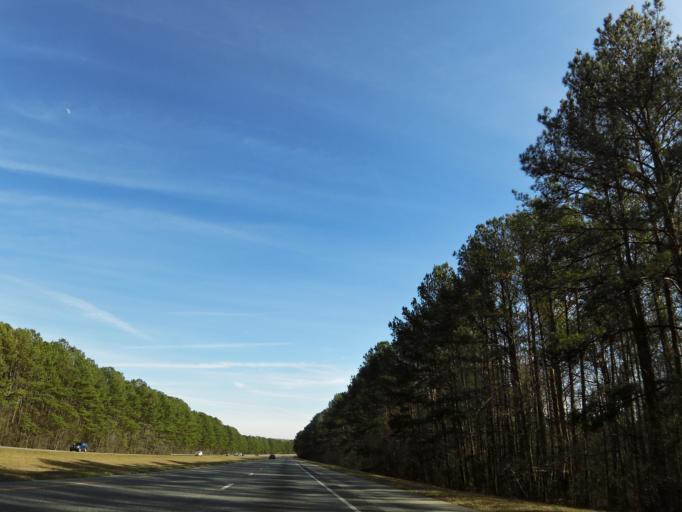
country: US
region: Georgia
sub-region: Harris County
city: Hamilton
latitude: 32.6982
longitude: -85.0021
